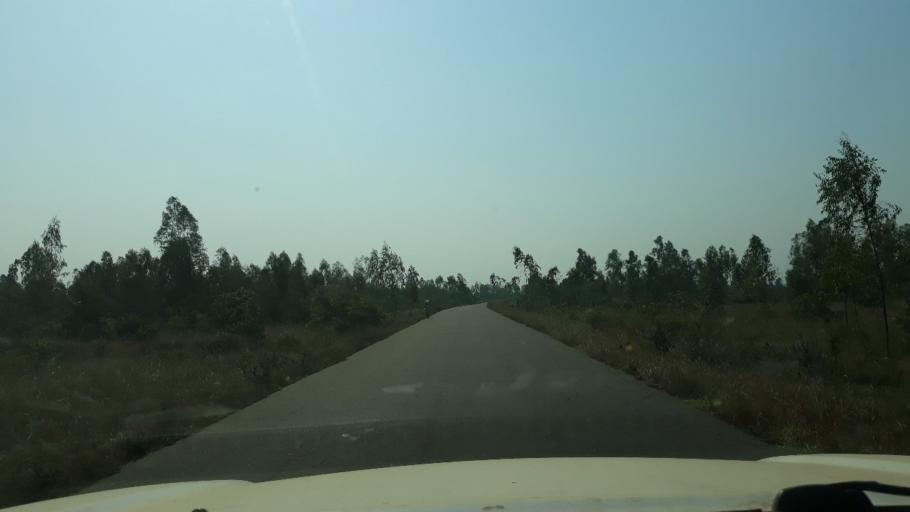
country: BI
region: Cibitoke
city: Cibitoke
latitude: -2.9513
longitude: 29.0727
